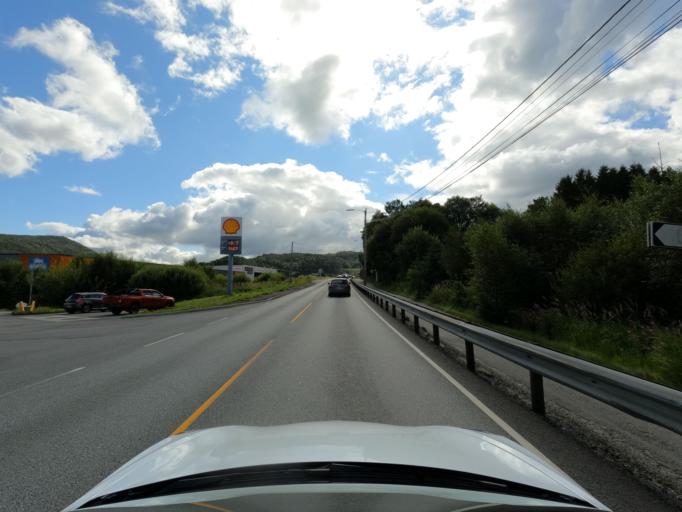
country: NO
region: Hordaland
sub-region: Bergen
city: Hylkje
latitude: 60.4886
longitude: 5.3767
